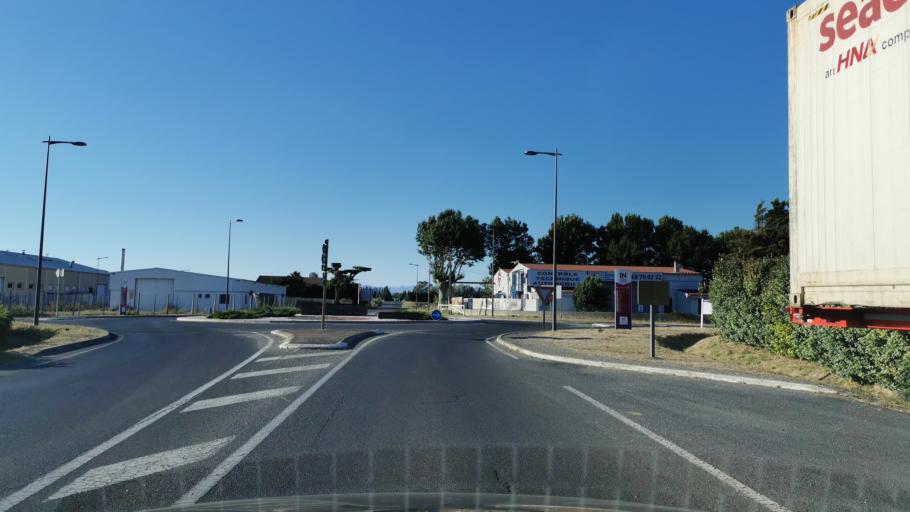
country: FR
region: Languedoc-Roussillon
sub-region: Departement de l'Aude
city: Ouveillan
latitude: 43.2518
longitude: 2.9968
